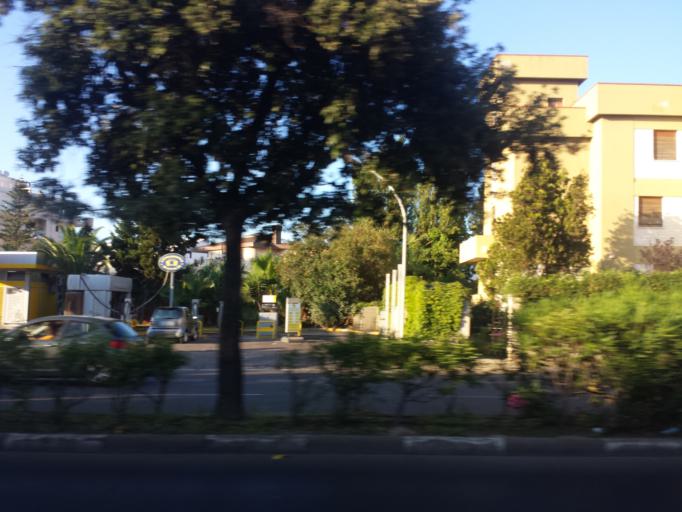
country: IT
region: Sardinia
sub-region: Provincia di Cagliari
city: Cagliari
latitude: 39.1954
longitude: 9.1531
